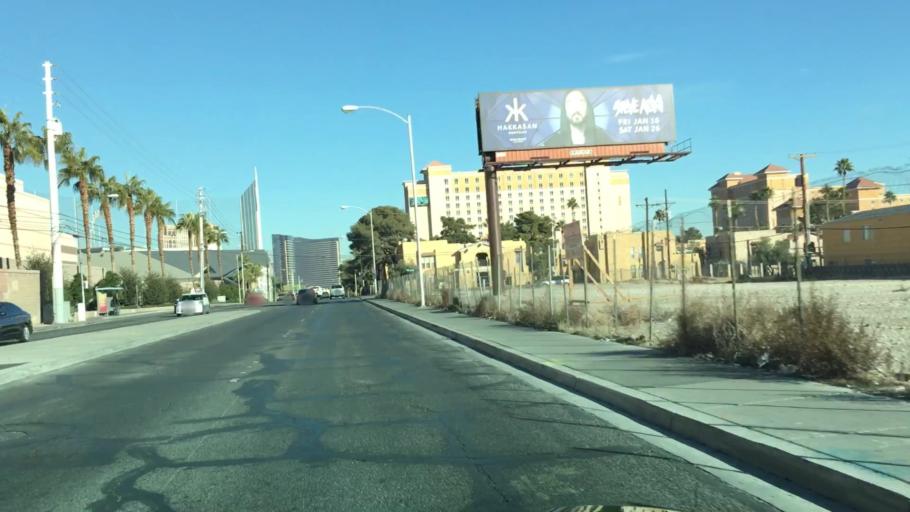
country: US
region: Nevada
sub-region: Clark County
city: Paradise
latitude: 36.1035
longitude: -115.1638
